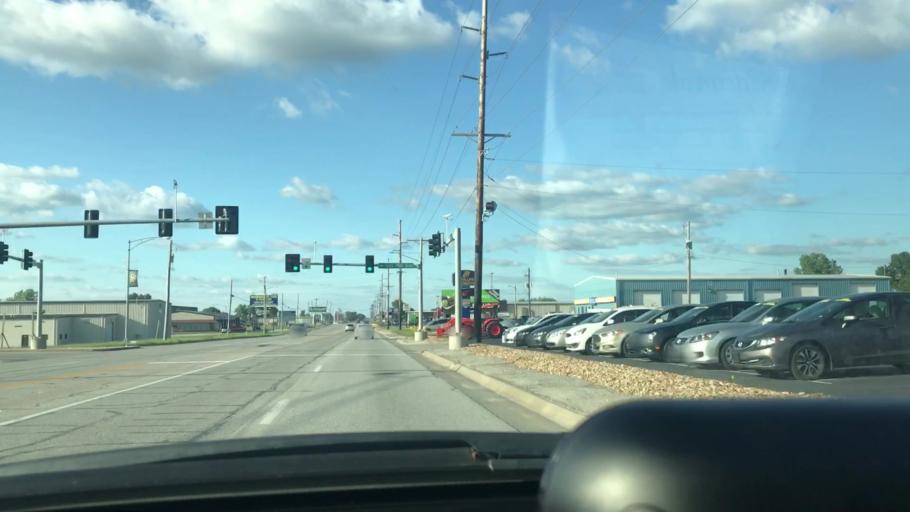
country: US
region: Missouri
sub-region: Pettis County
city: Sedalia
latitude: 38.6738
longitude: -93.2516
